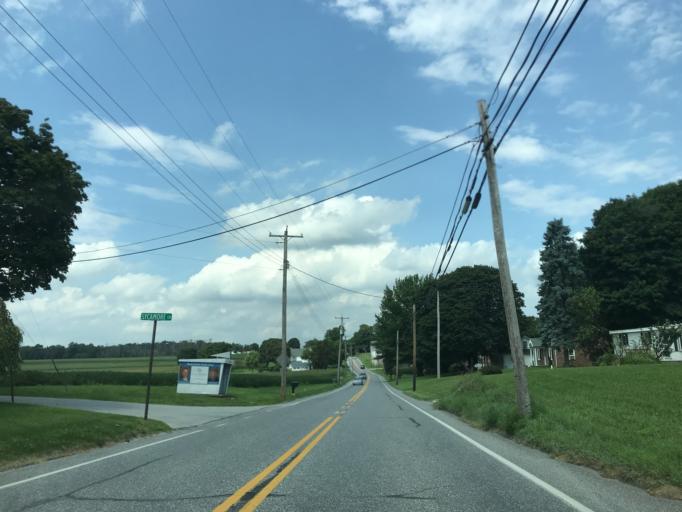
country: US
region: Pennsylvania
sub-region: York County
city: Red Lion
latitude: 39.8484
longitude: -76.6205
